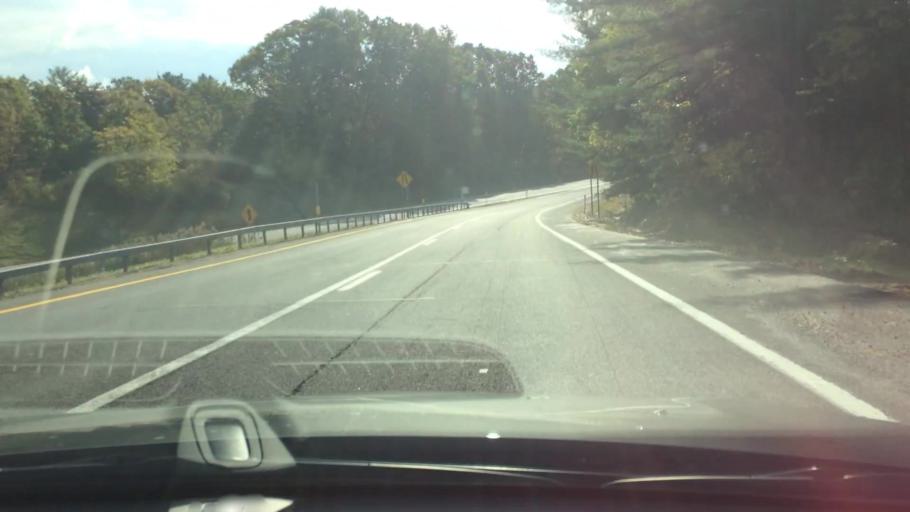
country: US
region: New York
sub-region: Saratoga County
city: Saratoga Springs
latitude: 43.0953
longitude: -73.7530
